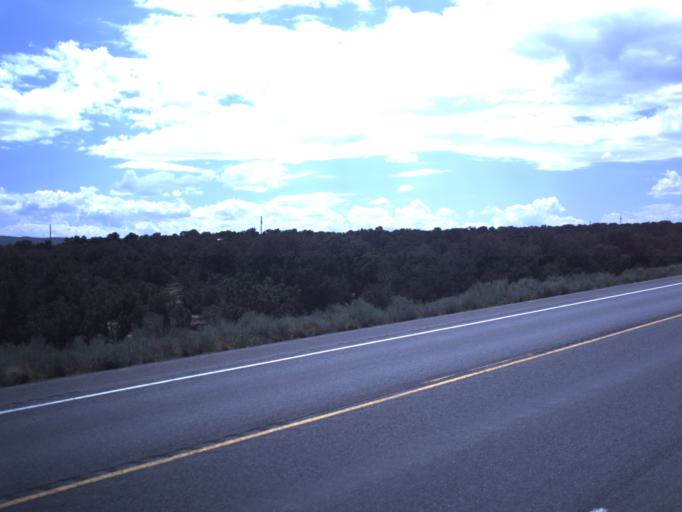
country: US
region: Utah
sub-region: Duchesne County
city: Duchesne
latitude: 40.1718
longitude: -110.5607
